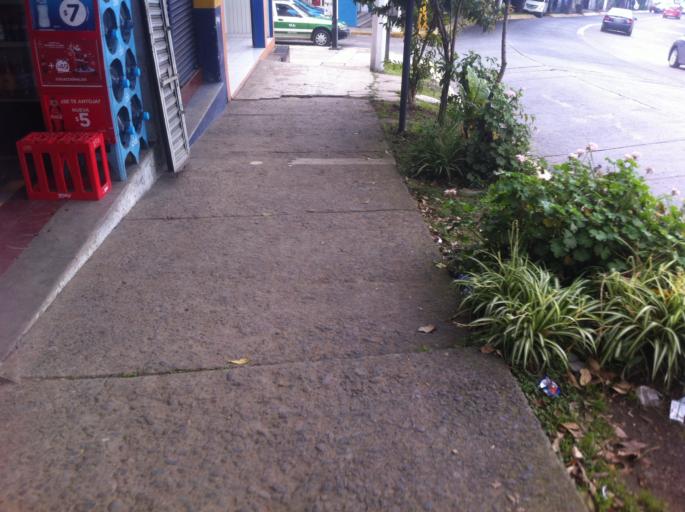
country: MX
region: Veracruz
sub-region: Xalapa
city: Xalapa de Enriquez
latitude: 19.5354
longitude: -96.9171
